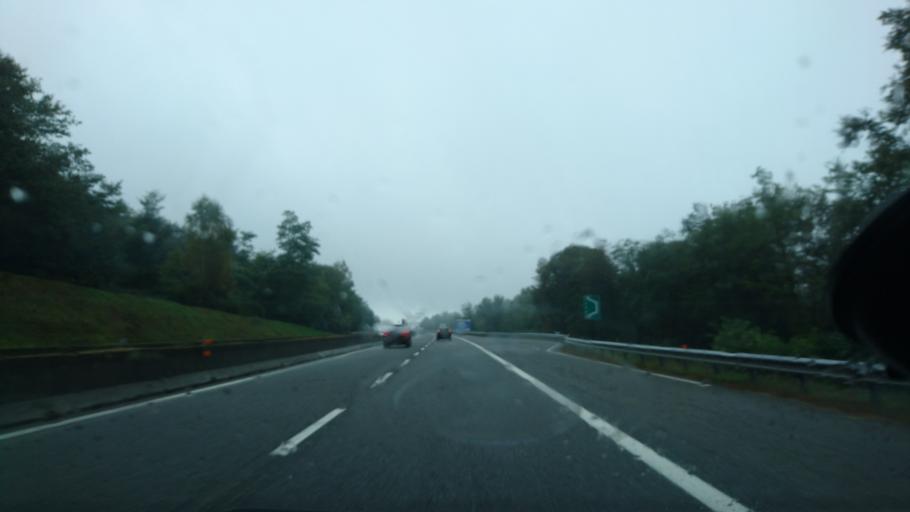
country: IT
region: Piedmont
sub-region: Provincia di Novara
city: Gattico
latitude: 45.7249
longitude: 8.5204
